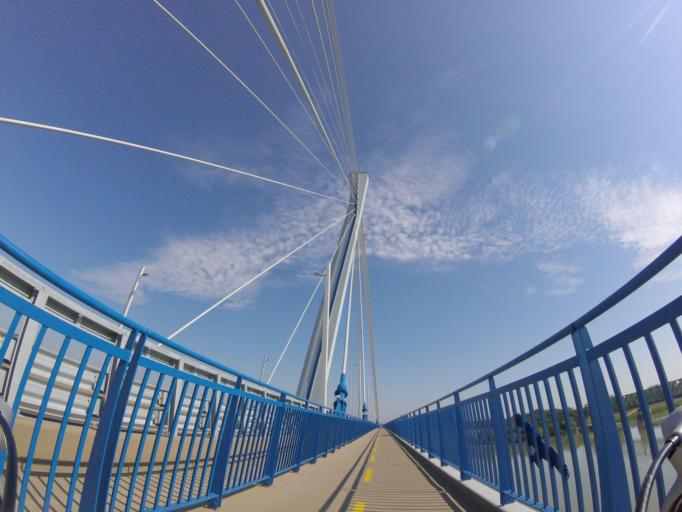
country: HU
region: Komarom-Esztergom
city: Komarom
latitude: 47.7566
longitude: 18.0847
